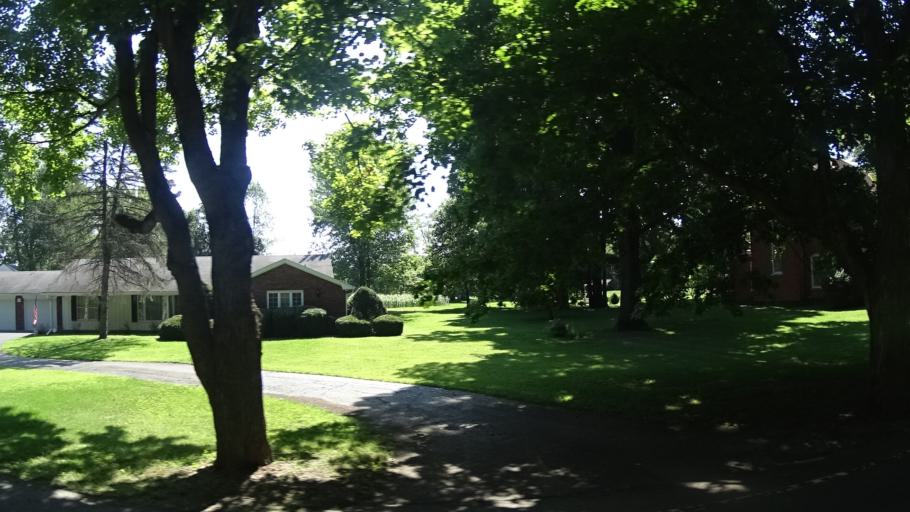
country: US
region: Indiana
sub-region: Madison County
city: Pendleton
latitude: 39.9924
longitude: -85.7486
